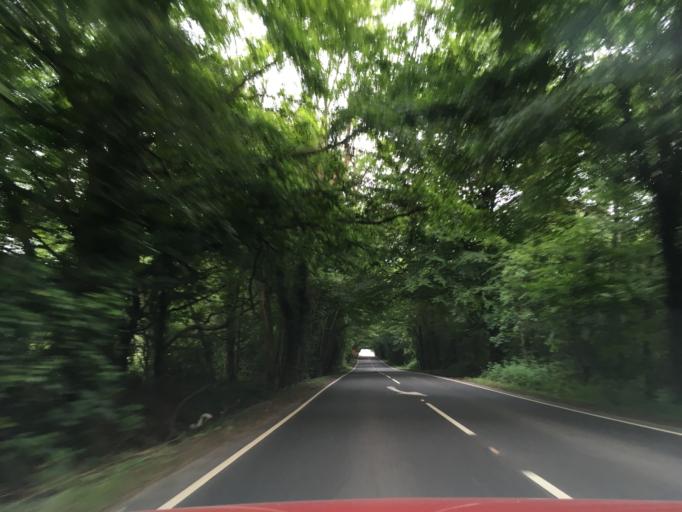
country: GB
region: England
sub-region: North Somerset
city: Long Ashton
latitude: 51.4429
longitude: -2.6800
